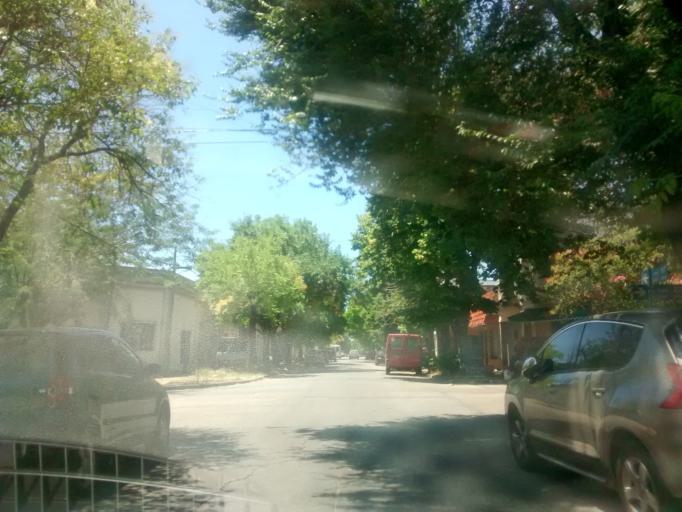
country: AR
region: Buenos Aires
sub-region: Partido de La Plata
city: La Plata
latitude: -34.9410
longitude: -57.9492
